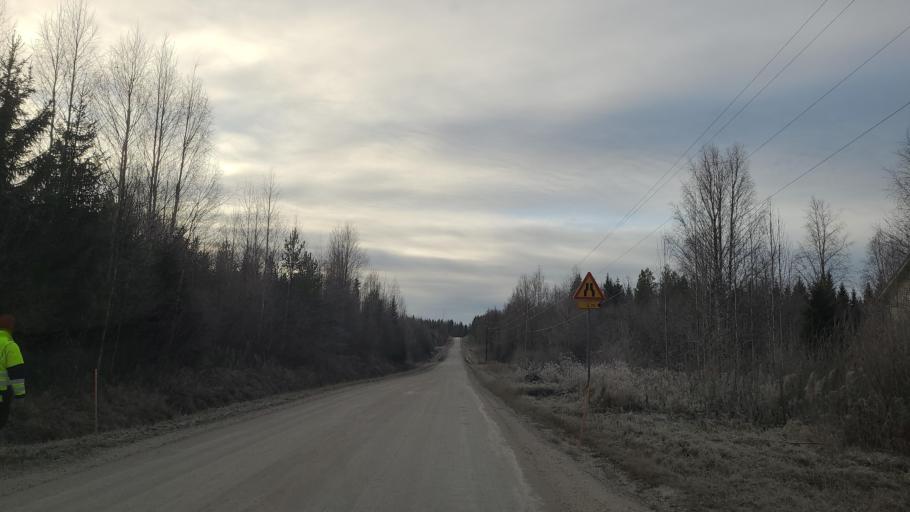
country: FI
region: Lapland
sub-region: Kemi-Tornio
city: Tervola
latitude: 66.0726
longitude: 25.0851
